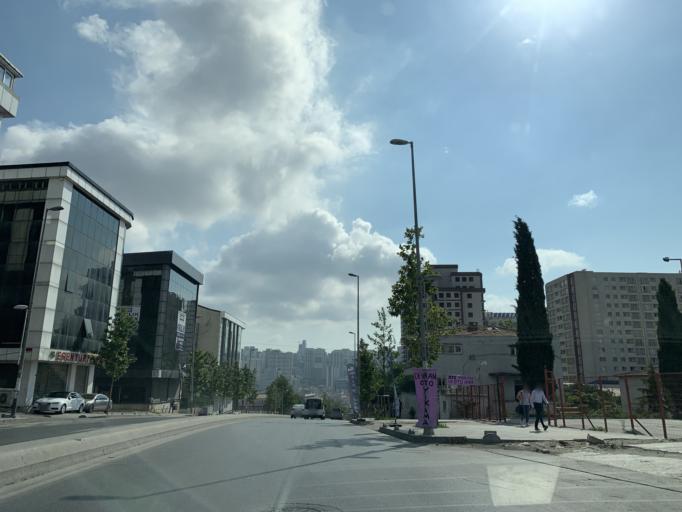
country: TR
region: Istanbul
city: Esenyurt
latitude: 41.0314
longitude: 28.6739
